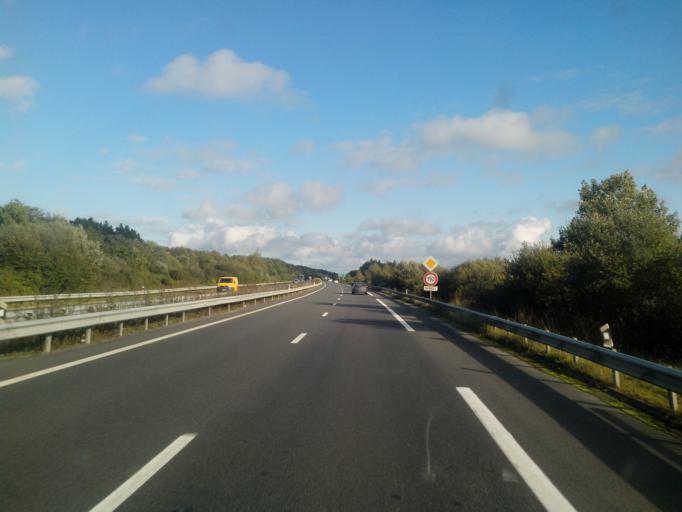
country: FR
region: Brittany
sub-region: Departement du Morbihan
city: Nivillac
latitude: 47.4993
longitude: -2.2600
